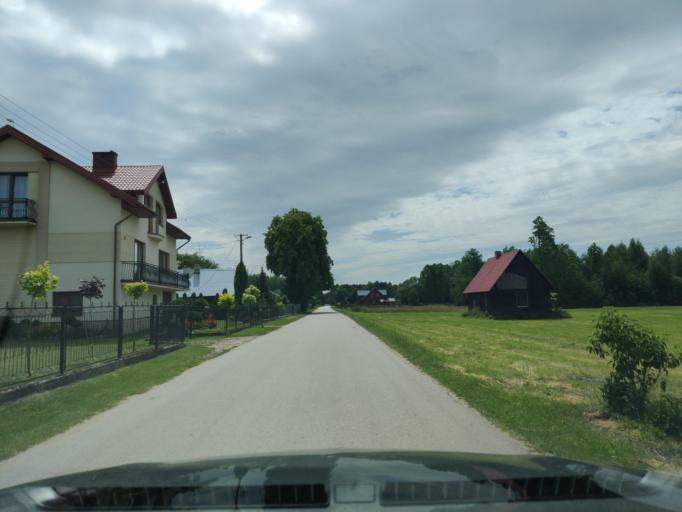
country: PL
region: Masovian Voivodeship
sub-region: Powiat pultuski
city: Obryte
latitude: 52.7356
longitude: 21.1699
